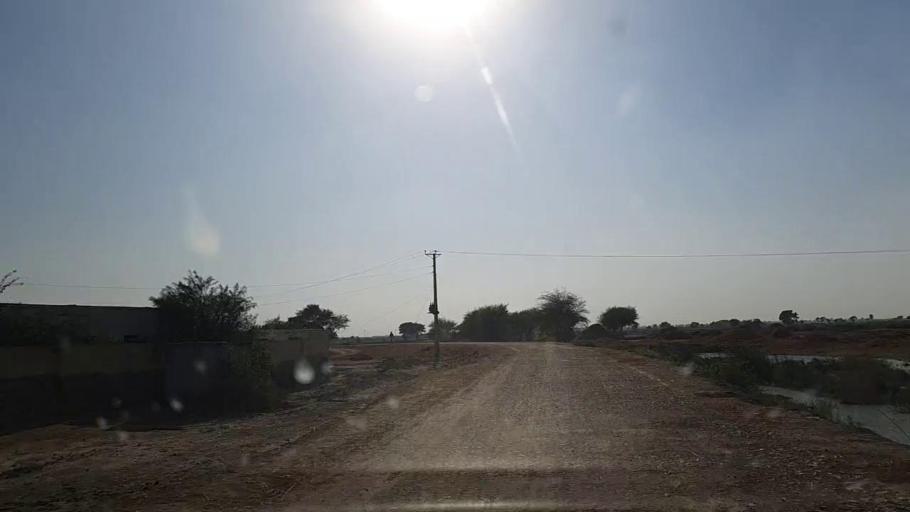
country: PK
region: Sindh
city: Thatta
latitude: 24.6225
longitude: 68.0786
